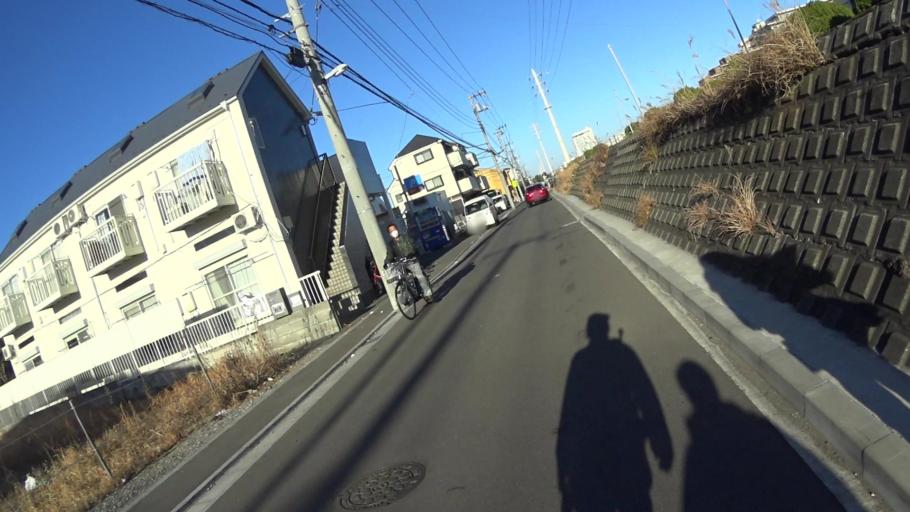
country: JP
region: Tokyo
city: Urayasu
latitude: 35.6394
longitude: 139.9089
